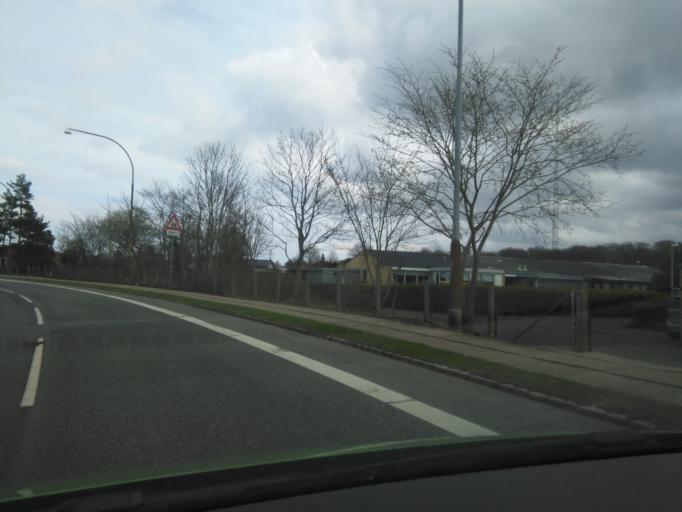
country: DK
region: South Denmark
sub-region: Nordfyns Kommune
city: Bogense
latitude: 55.5644
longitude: 10.0975
